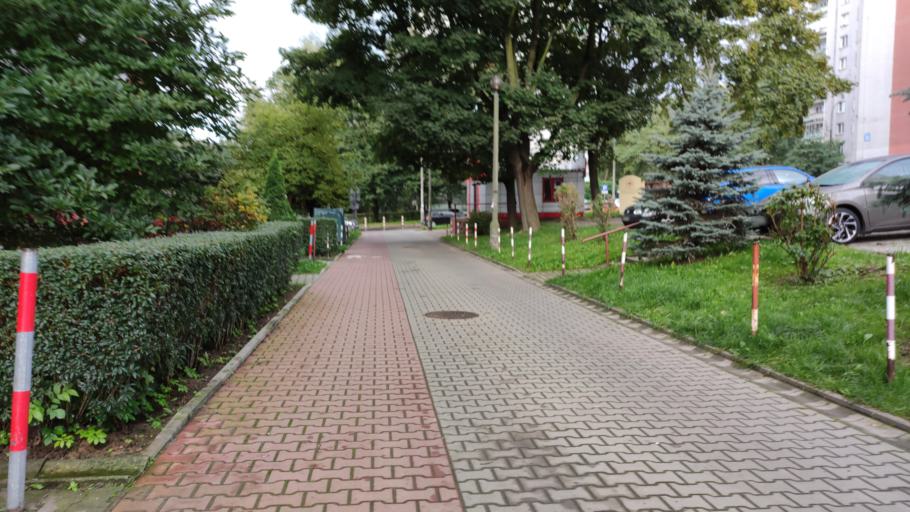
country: PL
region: Lesser Poland Voivodeship
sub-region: Powiat krakowski
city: Michalowice
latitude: 50.1006
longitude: 20.0150
